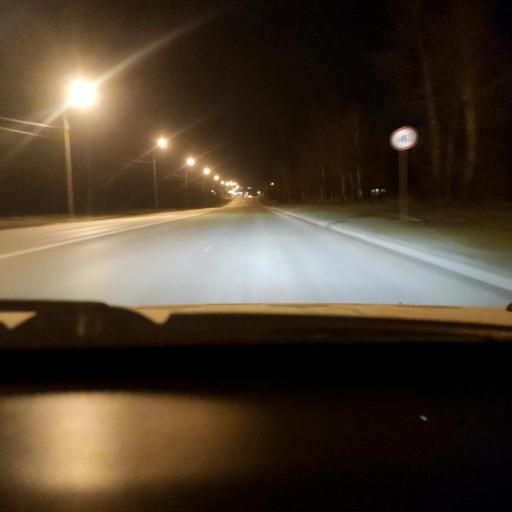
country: RU
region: Perm
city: Polazna
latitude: 58.1265
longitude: 56.4059
